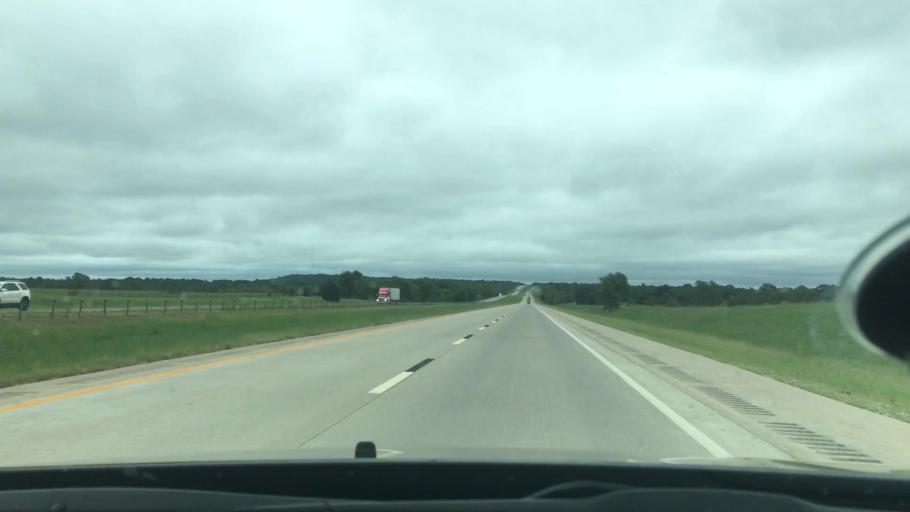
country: US
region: Oklahoma
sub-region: Muskogee County
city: Warner
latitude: 35.4822
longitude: -95.2653
